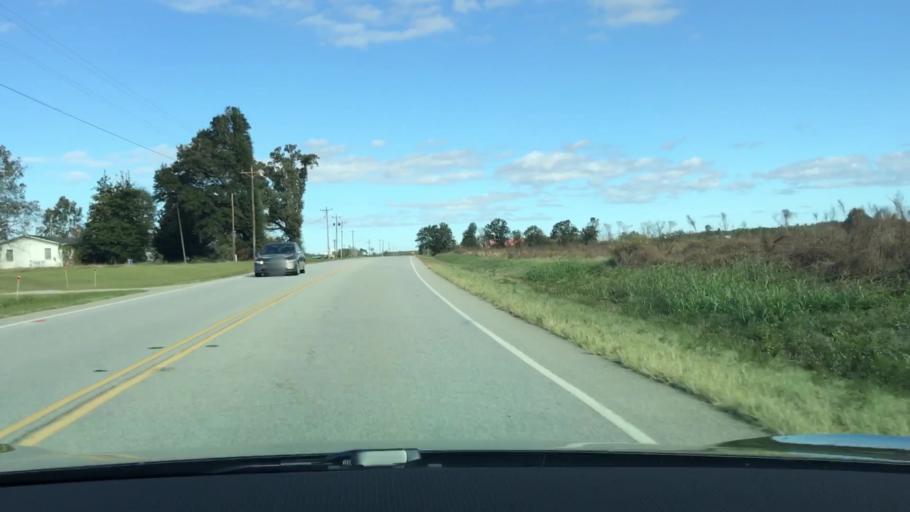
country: US
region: Georgia
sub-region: Jefferson County
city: Wrens
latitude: 33.1423
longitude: -82.4566
